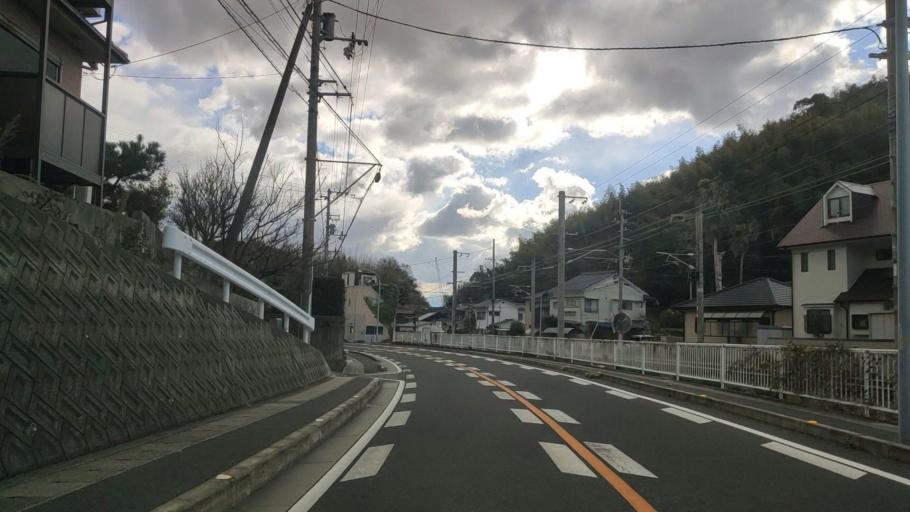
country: JP
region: Ehime
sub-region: Shikoku-chuo Shi
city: Matsuyama
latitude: 33.8702
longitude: 132.7109
